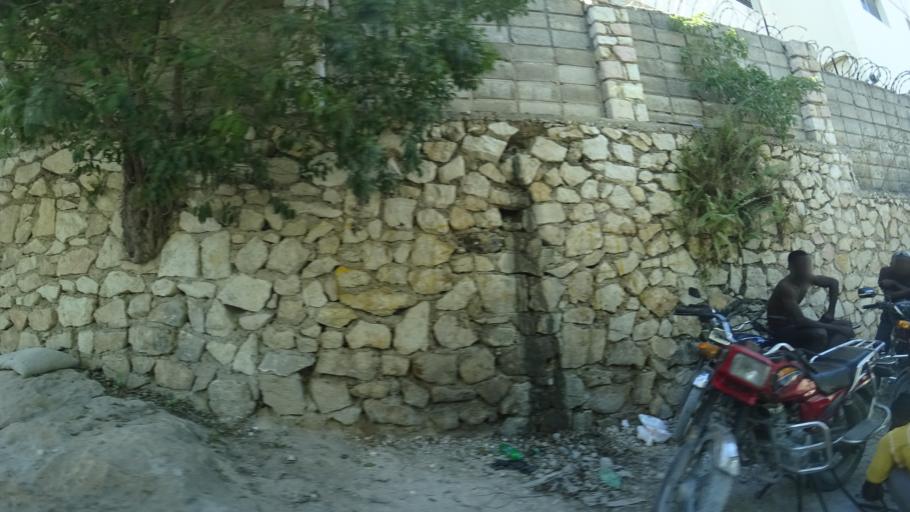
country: HT
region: Ouest
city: Delmas 73
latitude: 18.5379
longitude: -72.2848
